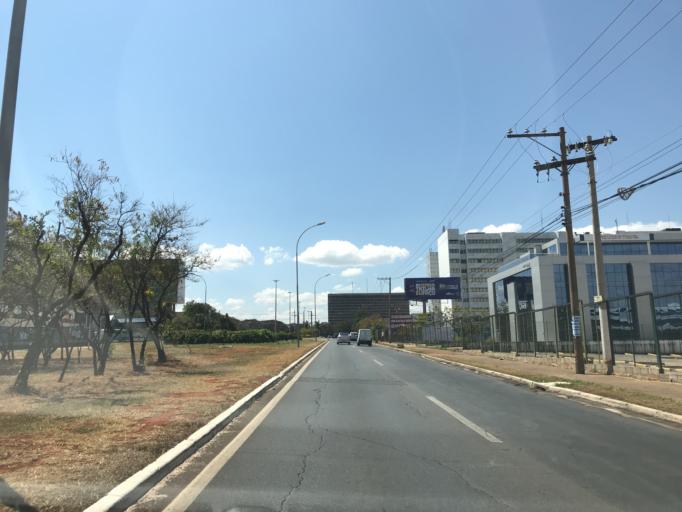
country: BR
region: Federal District
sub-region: Brasilia
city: Brasilia
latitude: -15.7896
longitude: -47.9107
